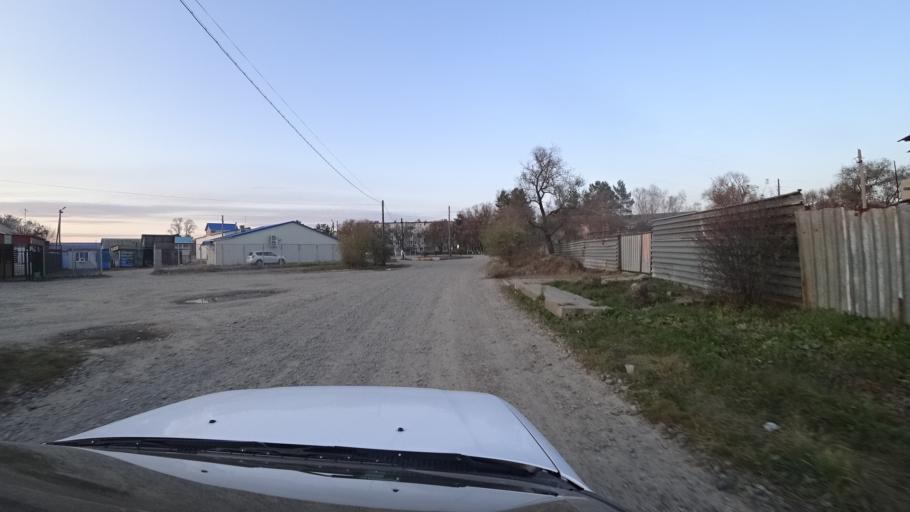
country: RU
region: Primorskiy
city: Dal'nerechensk
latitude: 45.9404
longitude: 133.8074
